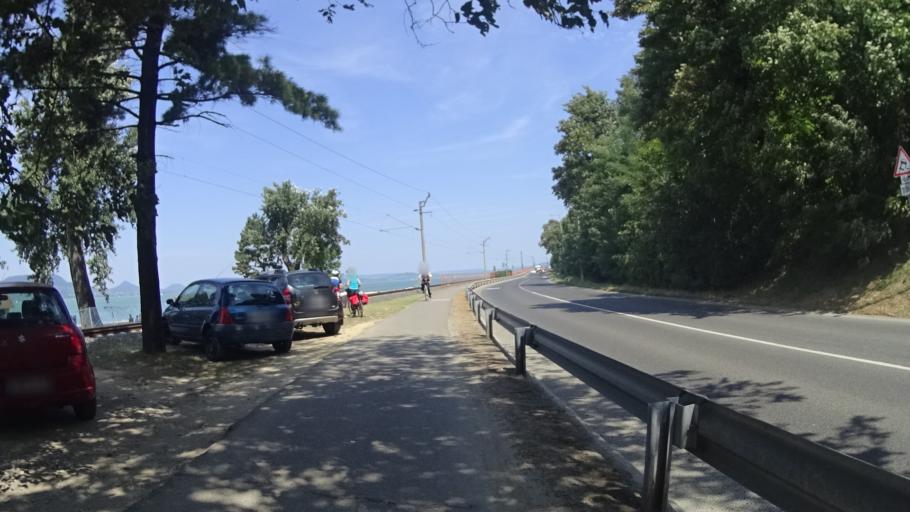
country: HU
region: Somogy
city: Fonyod
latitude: 46.7379
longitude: 17.5353
